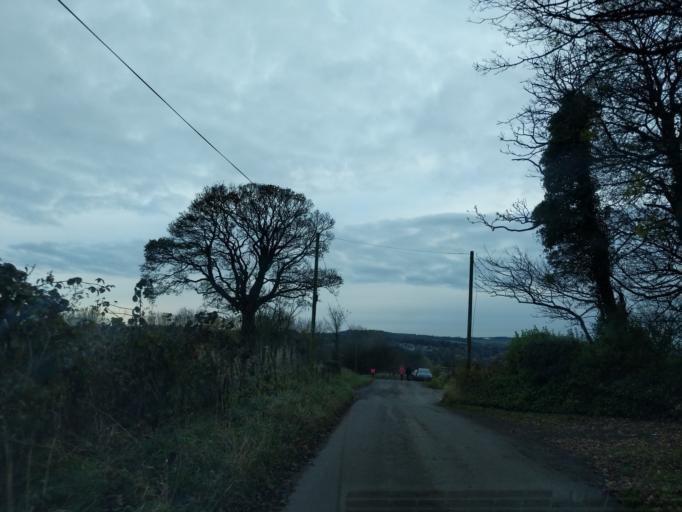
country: GB
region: Scotland
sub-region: West Lothian
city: Linlithgow
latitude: 55.9871
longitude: -3.5902
